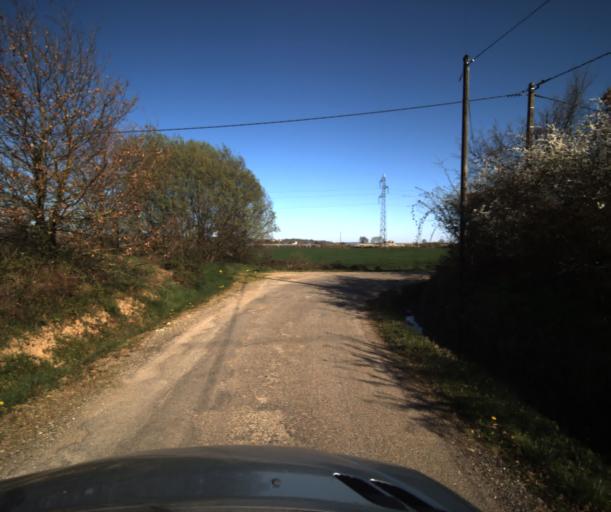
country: FR
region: Midi-Pyrenees
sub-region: Departement du Tarn-et-Garonne
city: Bressols
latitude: 43.9462
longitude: 1.3284
